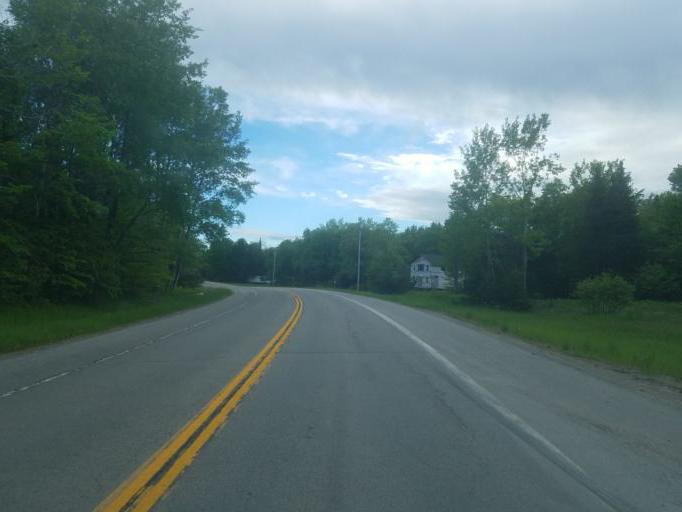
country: US
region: New York
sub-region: Herkimer County
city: Herkimer
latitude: 43.2721
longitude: -74.9851
